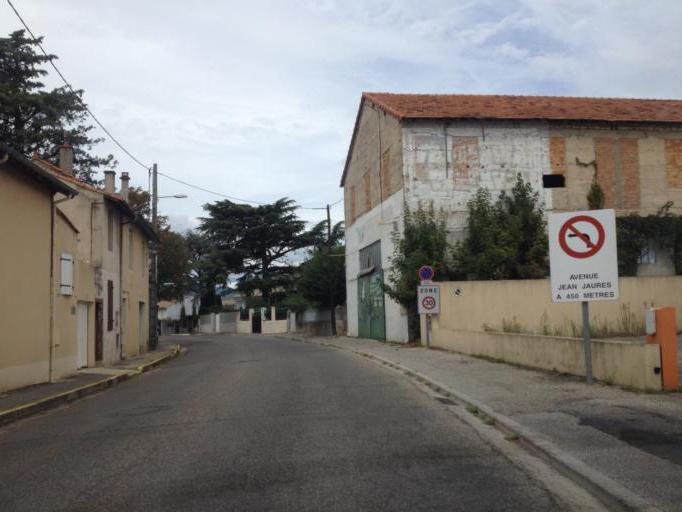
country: FR
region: Rhone-Alpes
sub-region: Departement de la Drome
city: Montelimar
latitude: 44.5491
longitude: 4.7521
